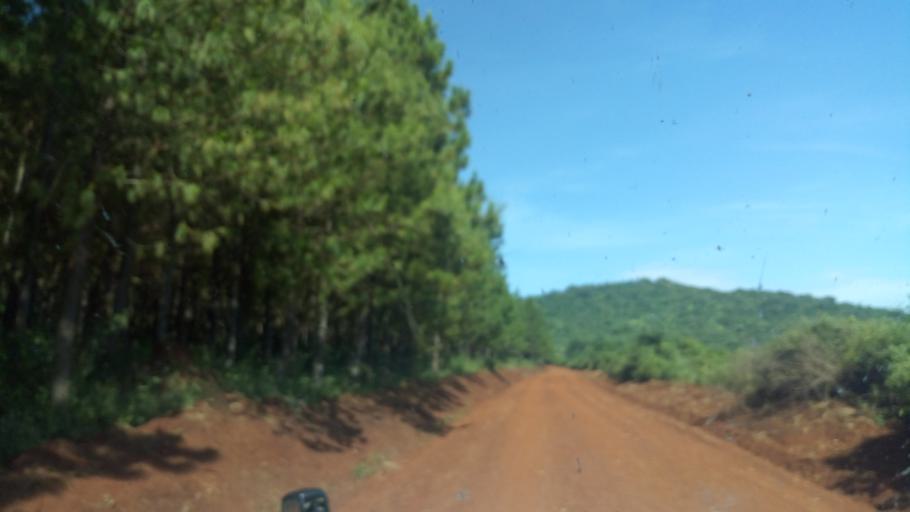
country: UG
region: Western Region
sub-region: Masindi District
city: Masindi
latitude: 1.6508
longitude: 31.7808
